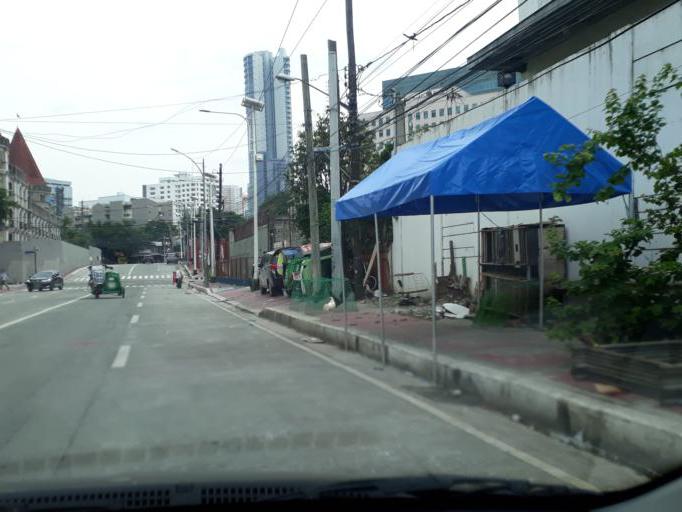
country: PH
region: Calabarzon
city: Del Monte
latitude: 14.6376
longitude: 121.0338
